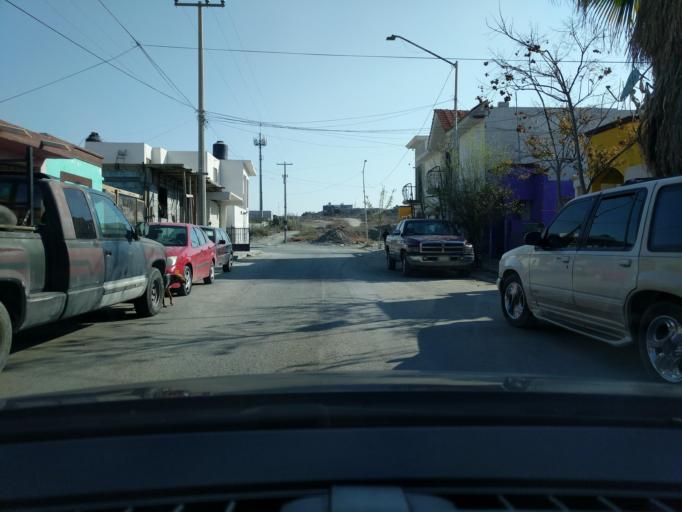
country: MX
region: Coahuila
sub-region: Ramos Arizpe
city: Ramos Arizpe
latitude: 25.5605
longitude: -100.9601
